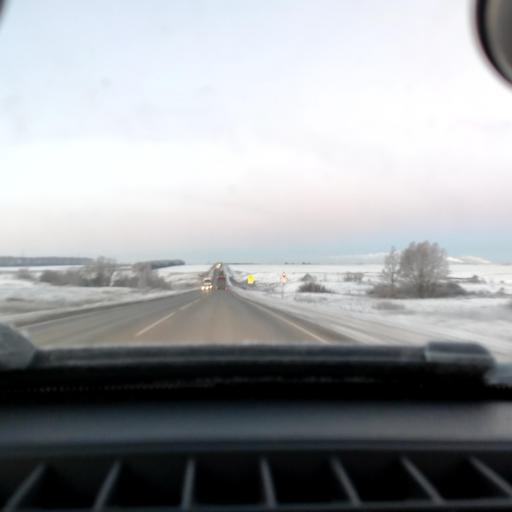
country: RU
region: Bashkortostan
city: Iglino
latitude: 54.7573
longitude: 56.3666
